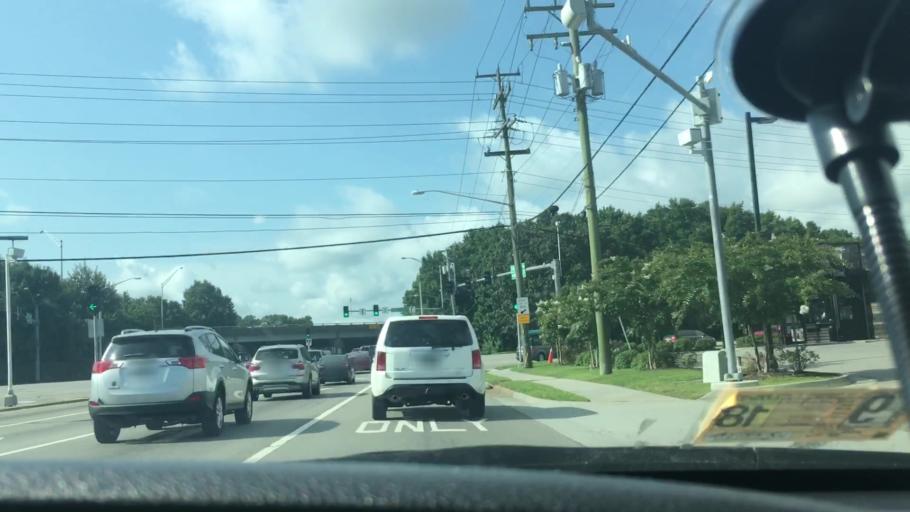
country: US
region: Virginia
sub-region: City of Virginia Beach
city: Virginia Beach
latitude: 36.8422
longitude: -76.0483
